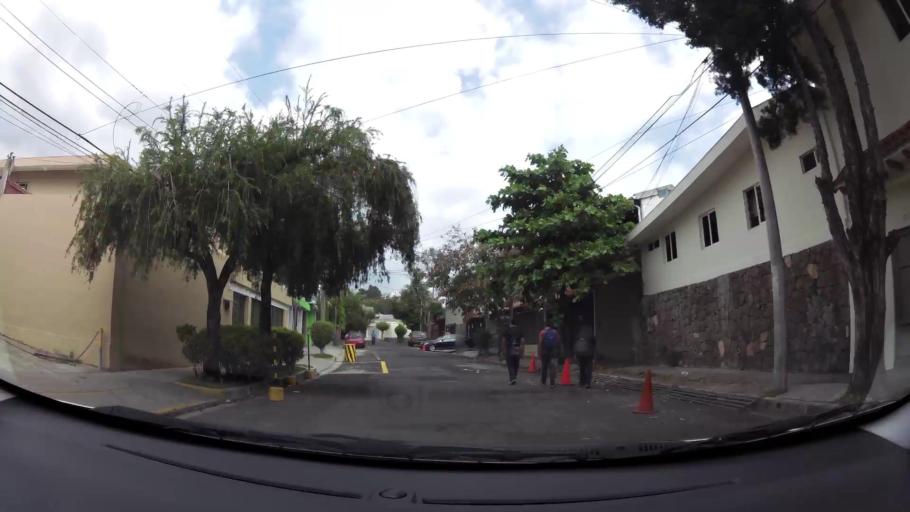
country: SV
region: La Libertad
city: Santa Tecla
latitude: 13.7085
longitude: -89.2505
